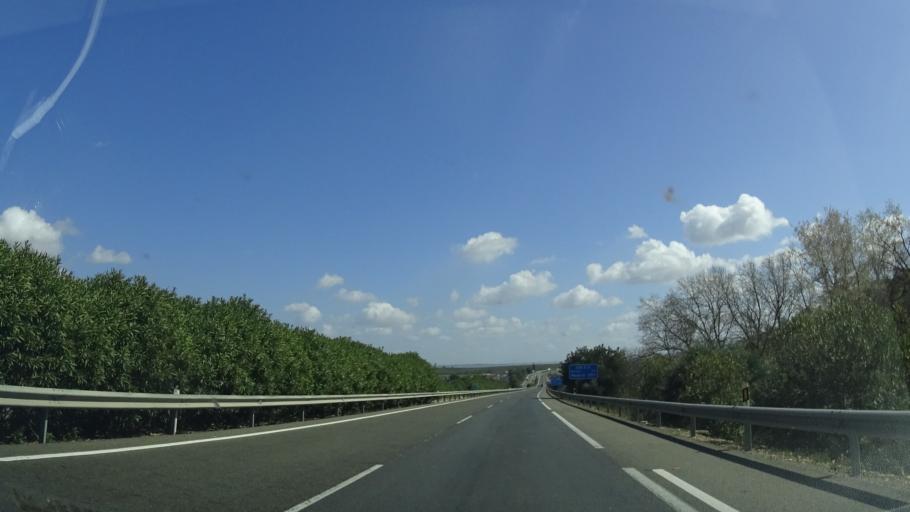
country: ES
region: Andalusia
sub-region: Province of Cordoba
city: Montoro
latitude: 38.0089
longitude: -4.3613
